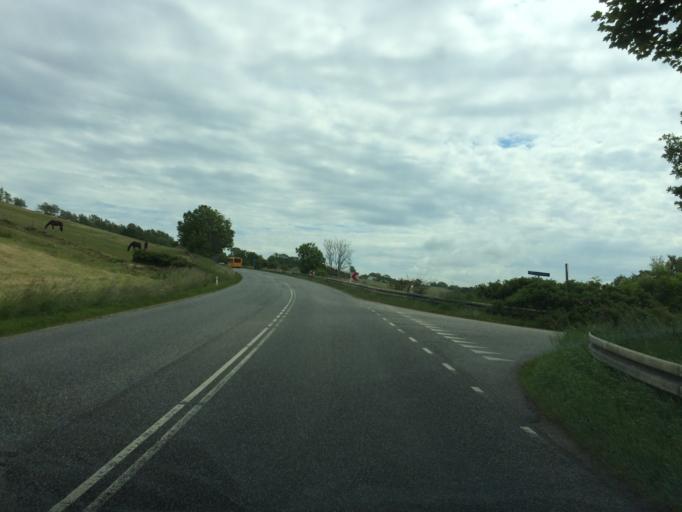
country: DK
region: Zealand
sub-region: Odsherred Kommune
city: Hojby
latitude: 55.9516
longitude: 11.4809
